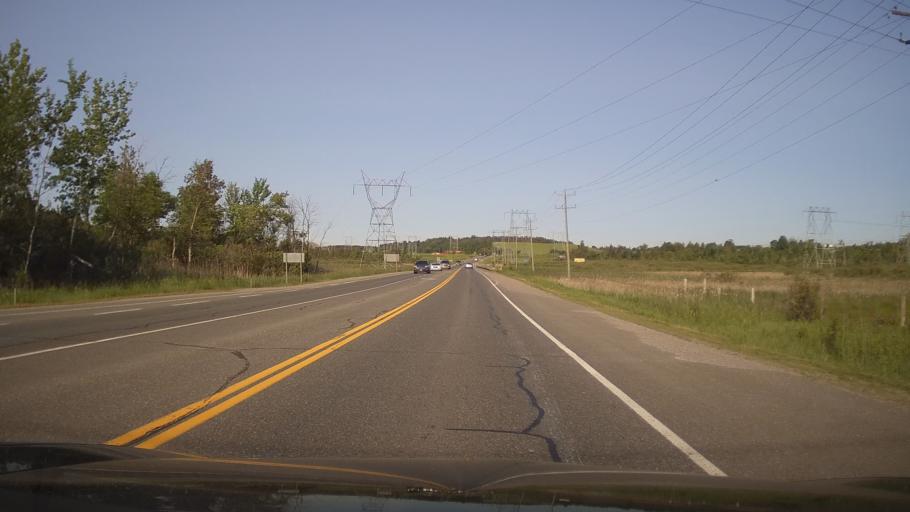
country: CA
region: Ontario
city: Peterborough
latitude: 44.3492
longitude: -78.0711
